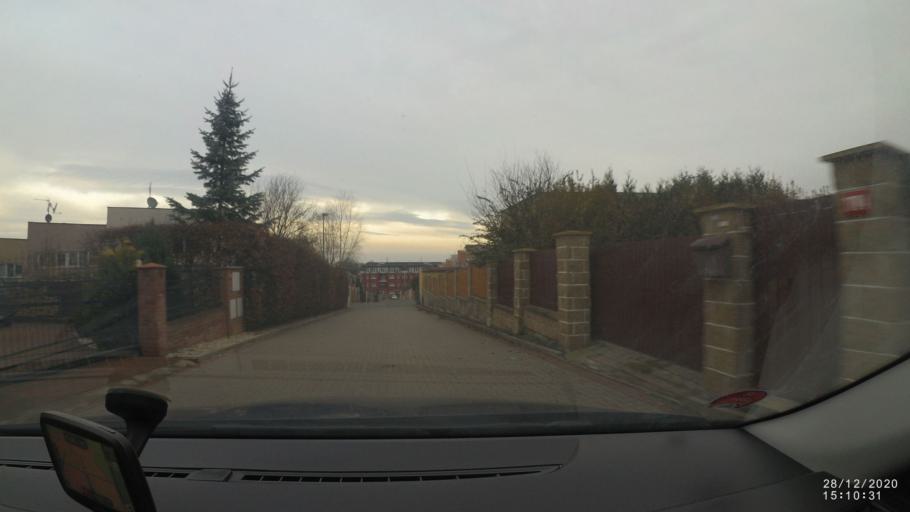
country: CZ
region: Central Bohemia
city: Uvaly
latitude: 50.0648
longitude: 14.7320
